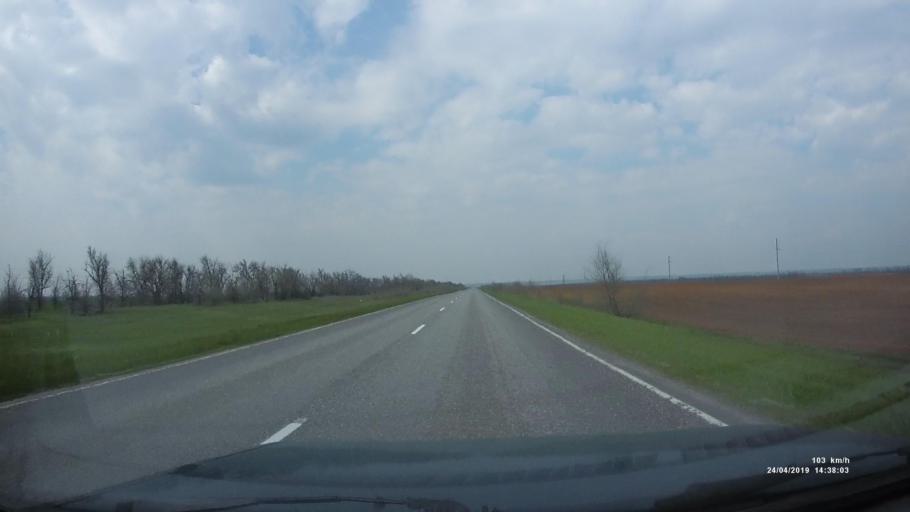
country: RU
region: Rostov
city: Remontnoye
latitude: 46.3953
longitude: 43.8863
